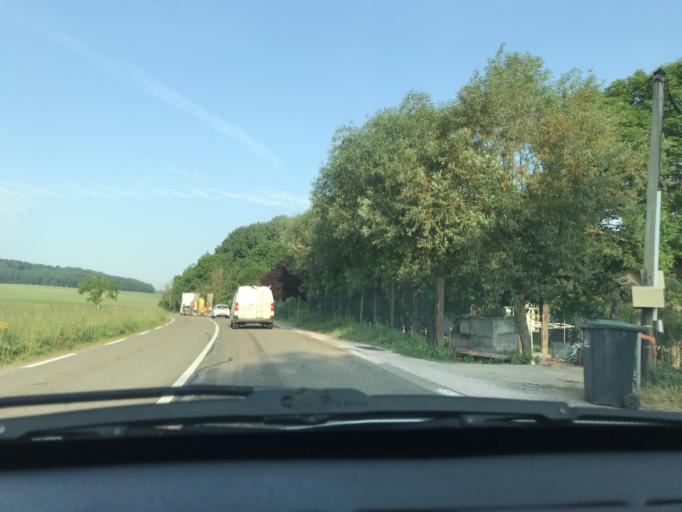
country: FR
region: Lorraine
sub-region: Departement de la Moselle
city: Vic-sur-Seille
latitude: 48.7803
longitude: 6.4920
